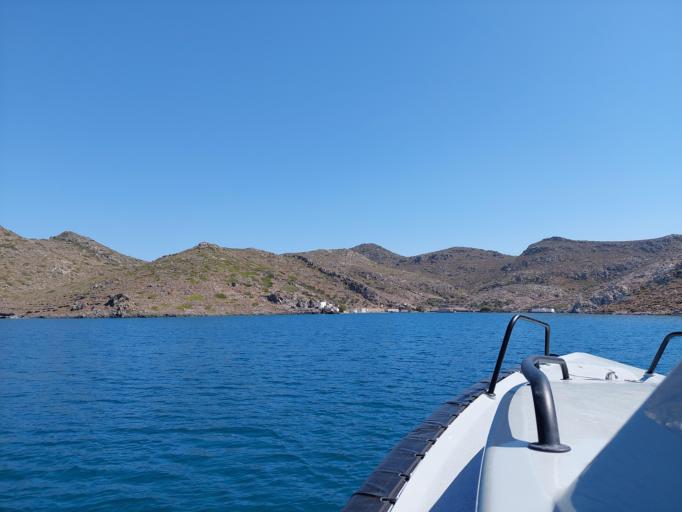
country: GR
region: South Aegean
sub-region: Nomos Dodekanisou
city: Karpathos
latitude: 35.8210
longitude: 27.2168
